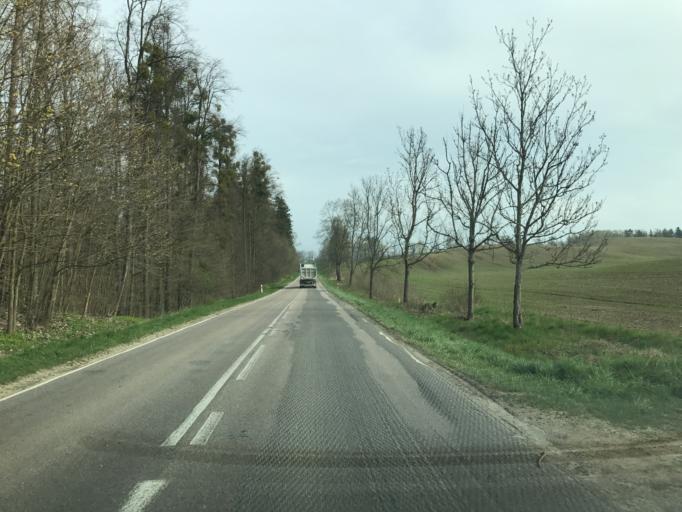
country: PL
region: Warmian-Masurian Voivodeship
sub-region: Powiat ostrodzki
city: Gierzwald
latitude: 53.5585
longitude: 20.0937
